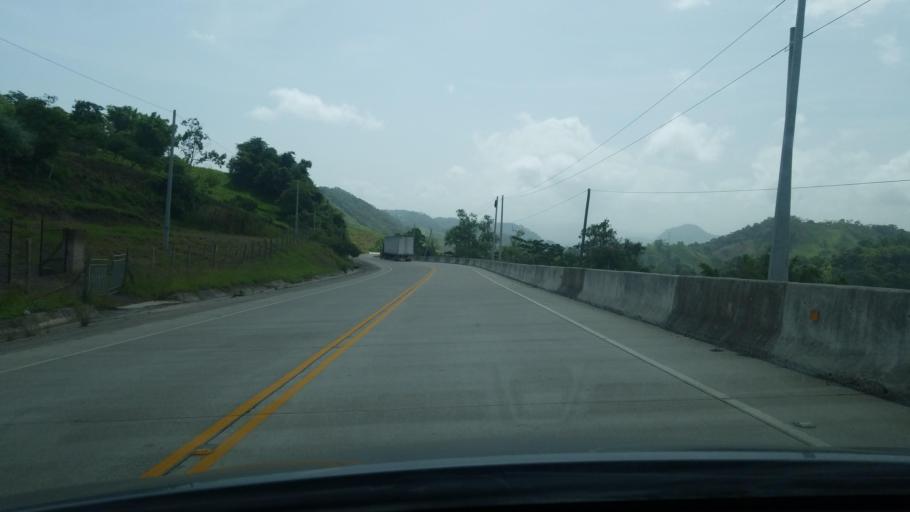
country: HN
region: Copan
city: San Jeronimo
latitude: 14.9553
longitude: -88.9027
